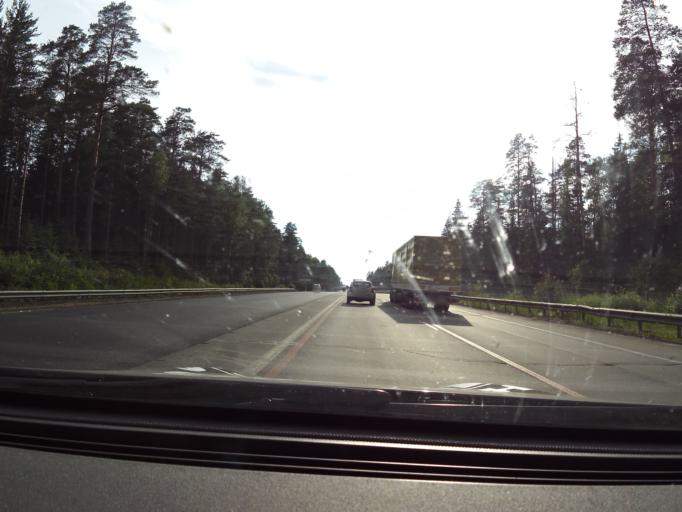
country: RU
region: Vladimir
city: Stepantsevo
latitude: 56.2314
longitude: 41.7573
